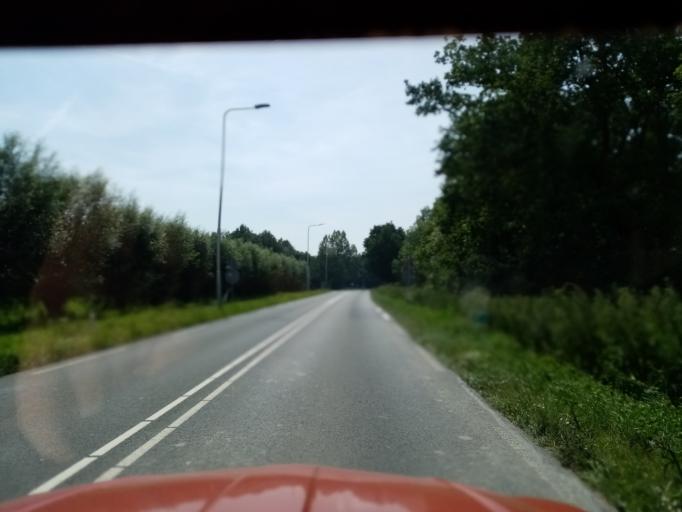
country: NL
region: South Holland
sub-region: Gemeente Alphen aan den Rijn
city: Alphen aan den Rijn
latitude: 52.1469
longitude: 4.7055
